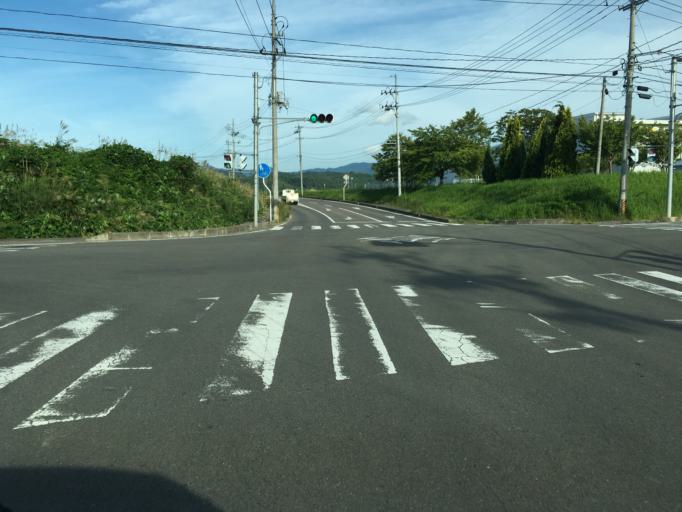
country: JP
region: Fukushima
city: Hobaramachi
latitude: 37.8085
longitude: 140.5583
